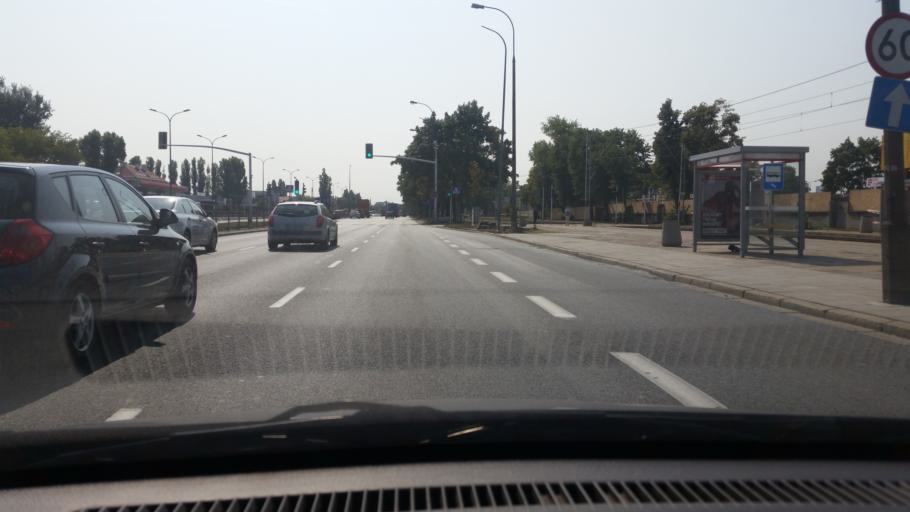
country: PL
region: Masovian Voivodeship
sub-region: Warszawa
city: Zoliborz
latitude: 52.2784
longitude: 21.0119
